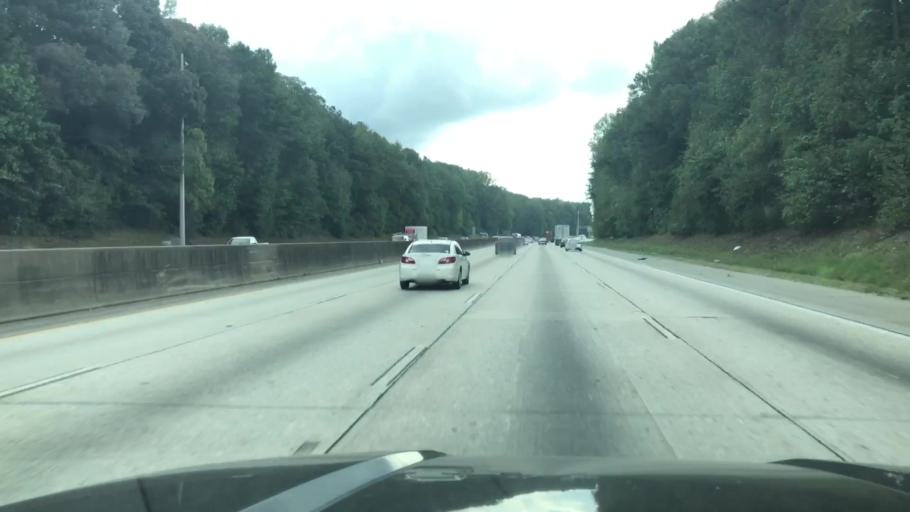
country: US
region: Georgia
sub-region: Fulton County
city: East Point
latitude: 33.7131
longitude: -84.5002
